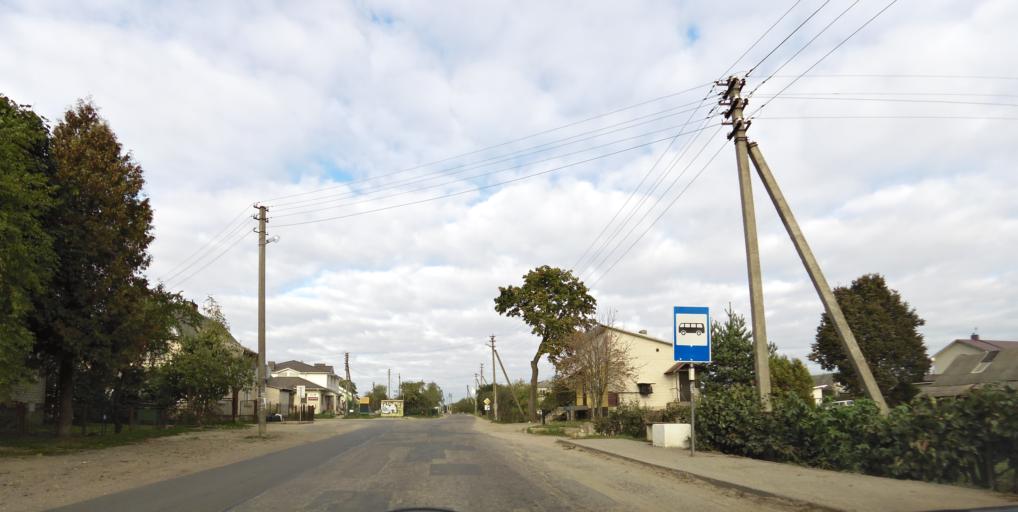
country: LT
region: Vilnius County
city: Pilaite
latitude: 54.7265
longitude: 25.1822
